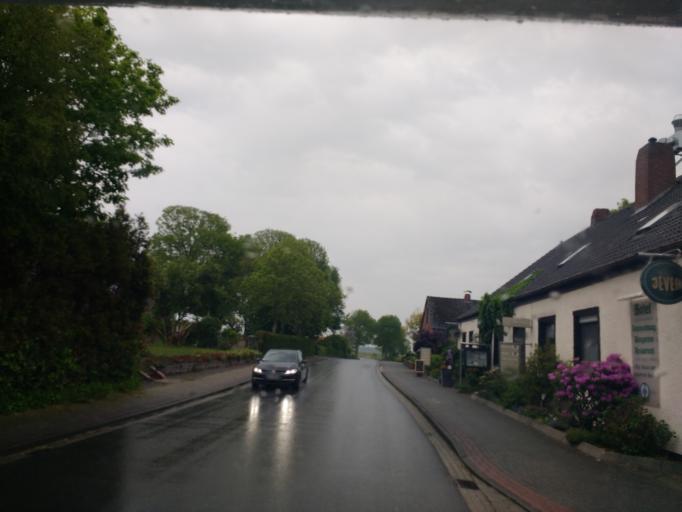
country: DE
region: Lower Saxony
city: Wangerooge
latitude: 53.6875
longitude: 7.8975
